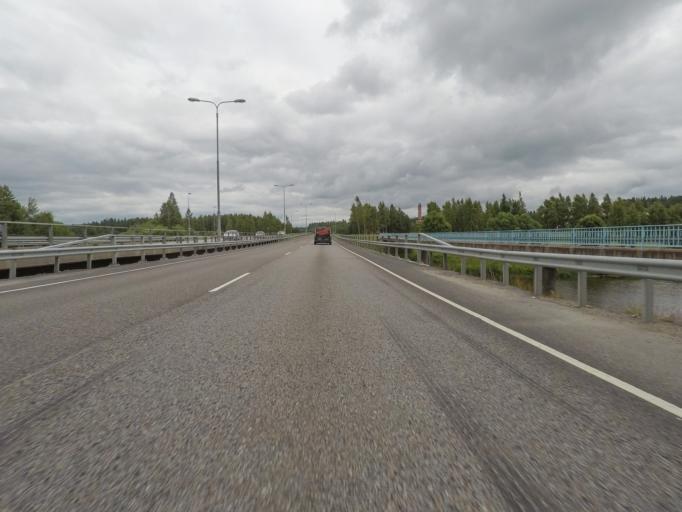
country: FI
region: Varsinais-Suomi
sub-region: Turku
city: Kaarina
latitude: 60.4729
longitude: 22.3572
